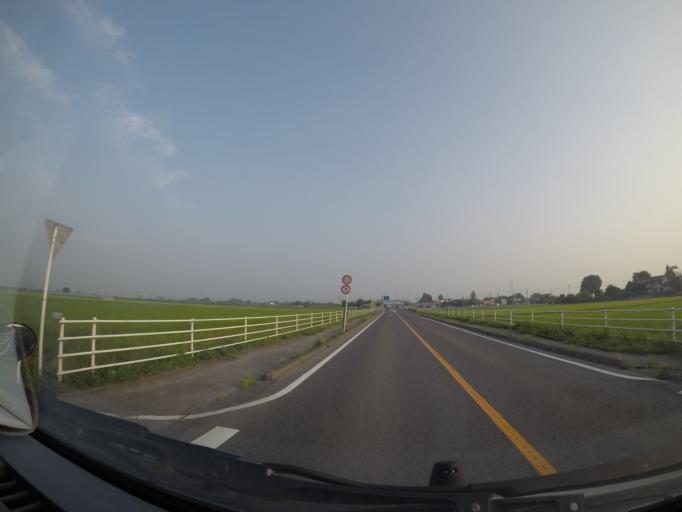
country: JP
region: Tochigi
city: Fujioka
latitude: 36.2508
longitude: 139.7143
